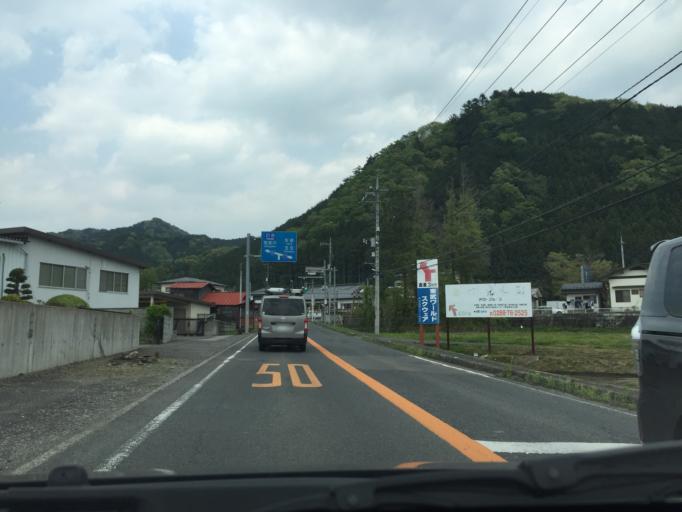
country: JP
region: Tochigi
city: Imaichi
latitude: 36.7801
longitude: 139.7120
